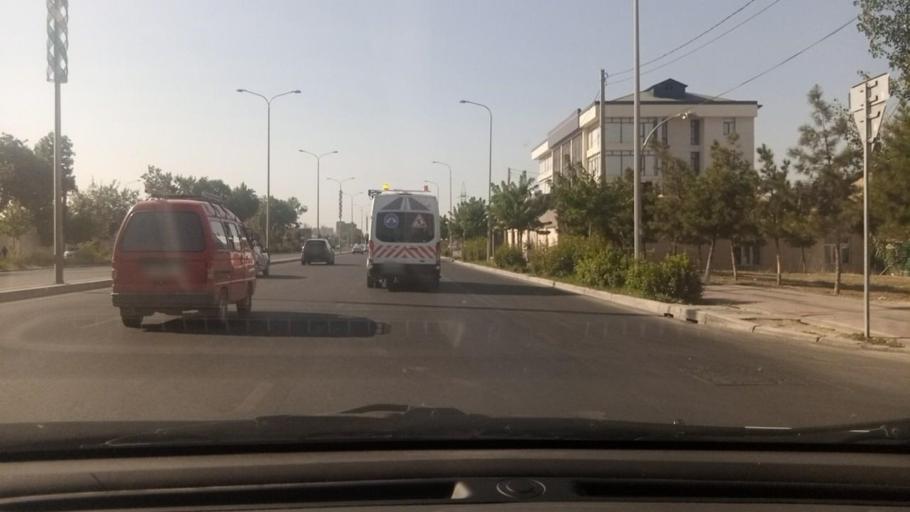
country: UZ
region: Toshkent Shahri
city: Bektemir
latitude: 41.2504
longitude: 69.3234
